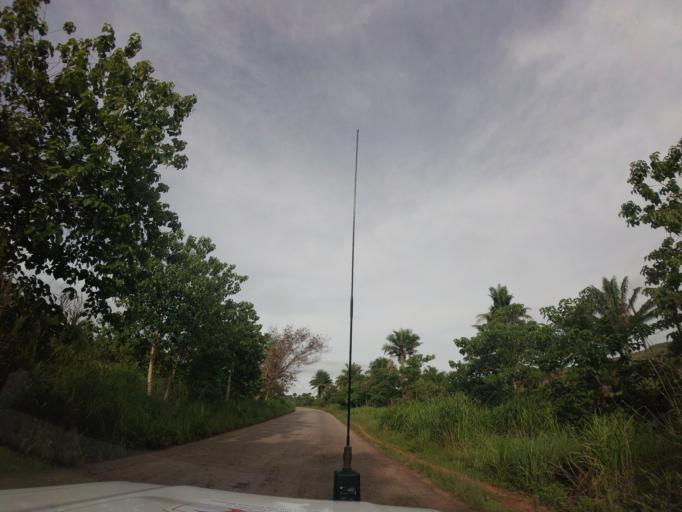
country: GN
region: Kindia
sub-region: Kindia
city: Kindia
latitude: 9.9212
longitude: -12.9960
